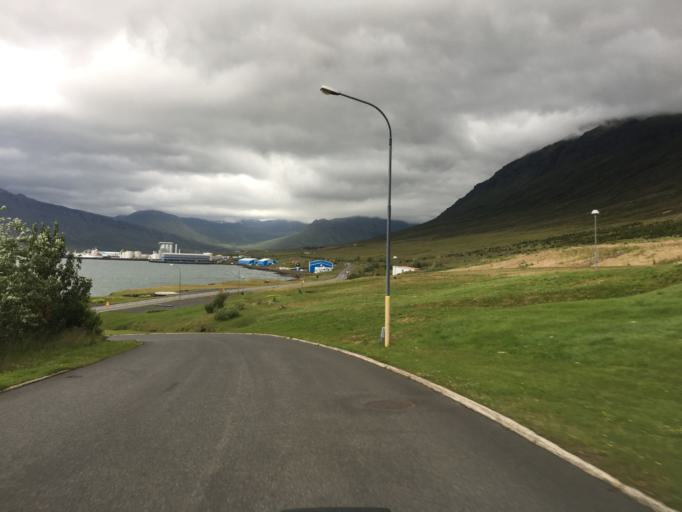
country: IS
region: East
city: Neskaupstadur
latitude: 65.1479
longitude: -13.7146
